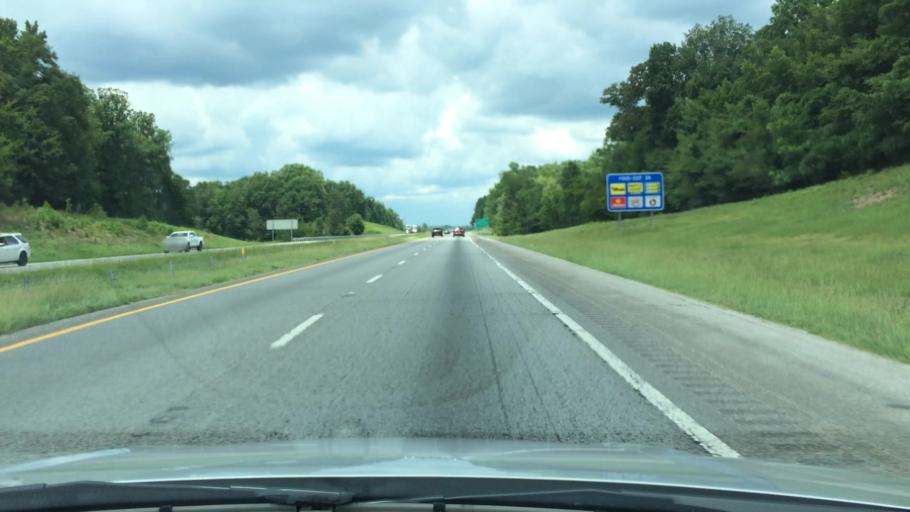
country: US
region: South Carolina
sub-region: Spartanburg County
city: Roebuck
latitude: 34.8246
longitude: -81.9650
